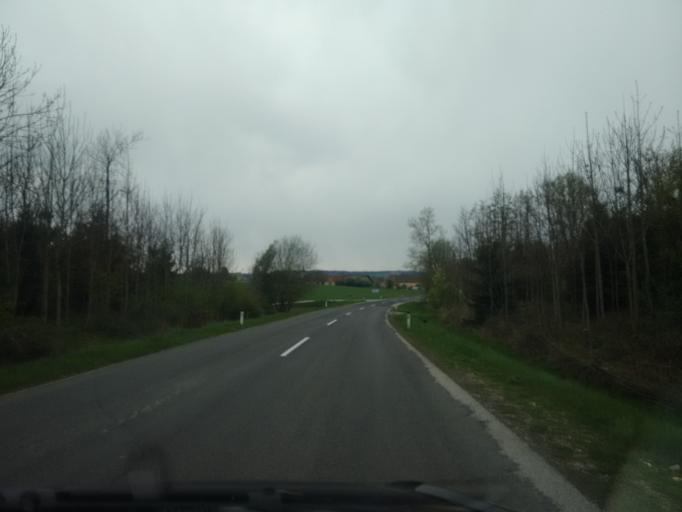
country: AT
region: Upper Austria
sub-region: Wels-Land
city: Buchkirchen
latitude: 48.2162
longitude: 14.0101
